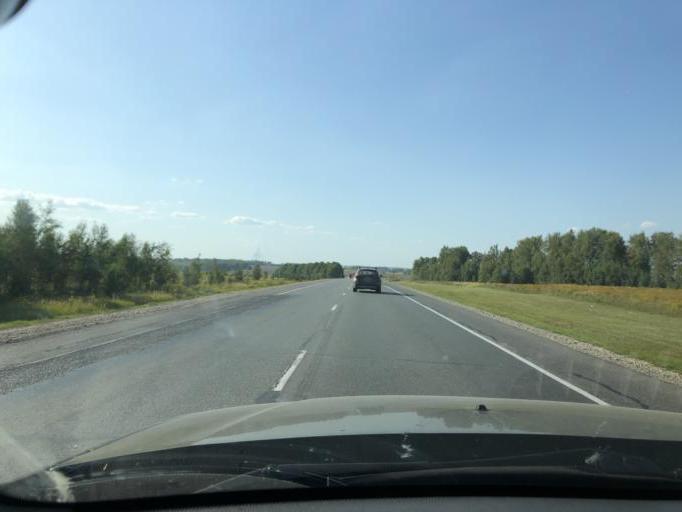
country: RU
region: Tula
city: Leninskiy
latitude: 54.2366
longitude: 37.3496
